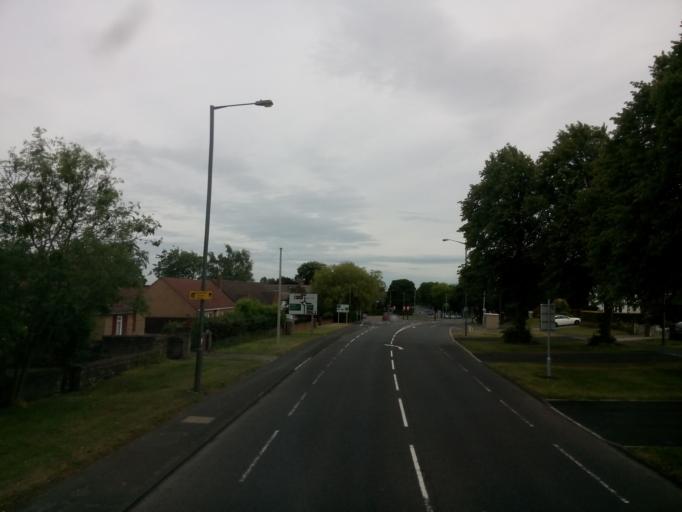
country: GB
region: England
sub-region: County Durham
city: Chester-le-Street
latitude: 54.8694
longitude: -1.5747
